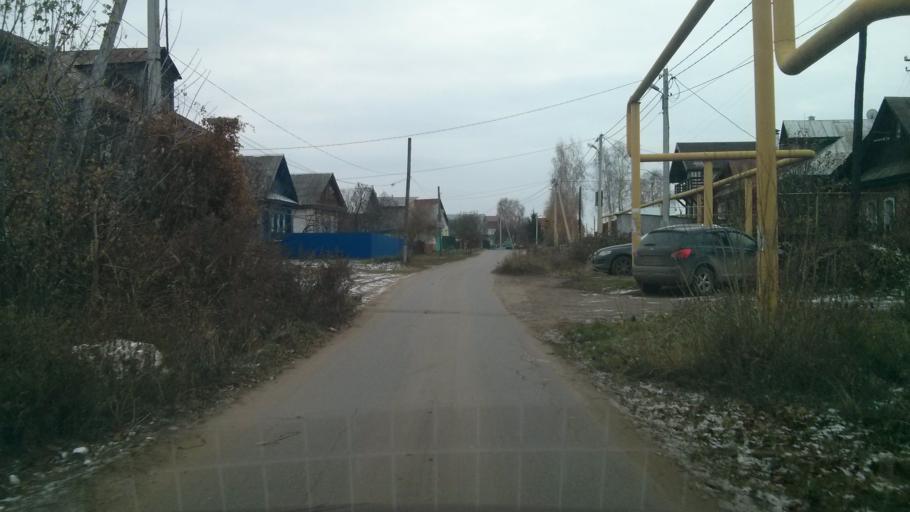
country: RU
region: Nizjnij Novgorod
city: Afonino
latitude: 56.3029
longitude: 44.0987
